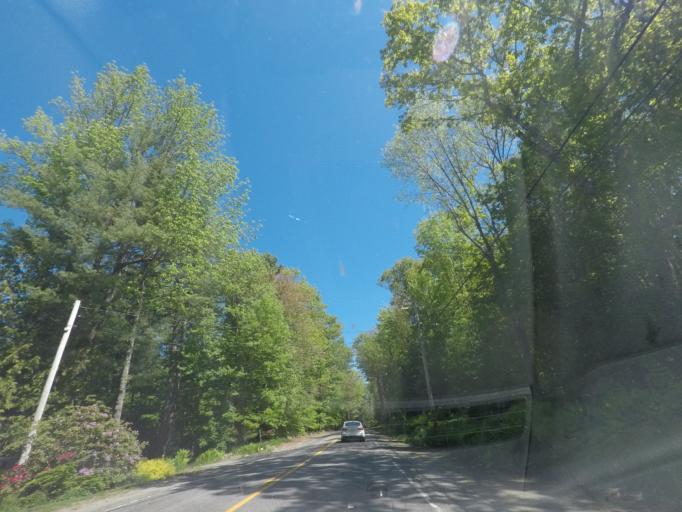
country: US
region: Maine
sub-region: Kennebec County
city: Manchester
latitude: 44.2956
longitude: -69.8881
